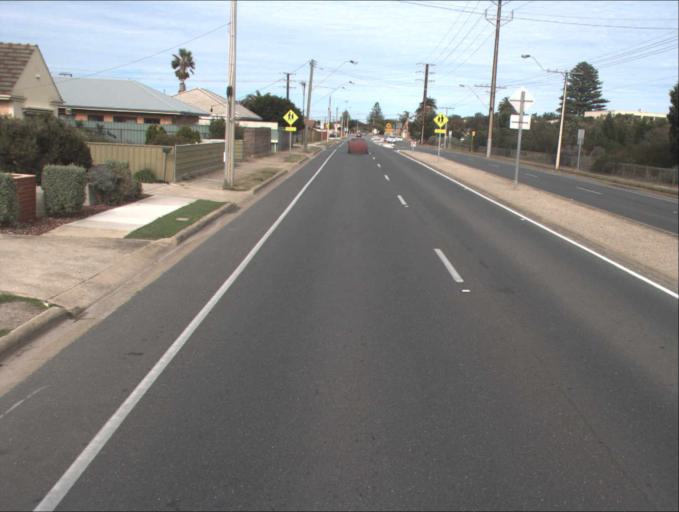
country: AU
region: South Australia
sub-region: Charles Sturt
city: West Lakes Shore
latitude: -34.8540
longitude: 138.4788
